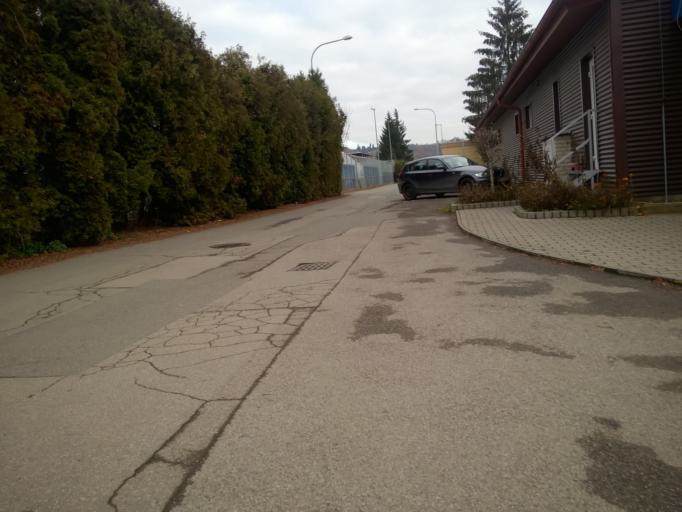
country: CZ
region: Praha
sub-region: Praha 1
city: Mala Strana
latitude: 50.1093
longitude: 14.4083
